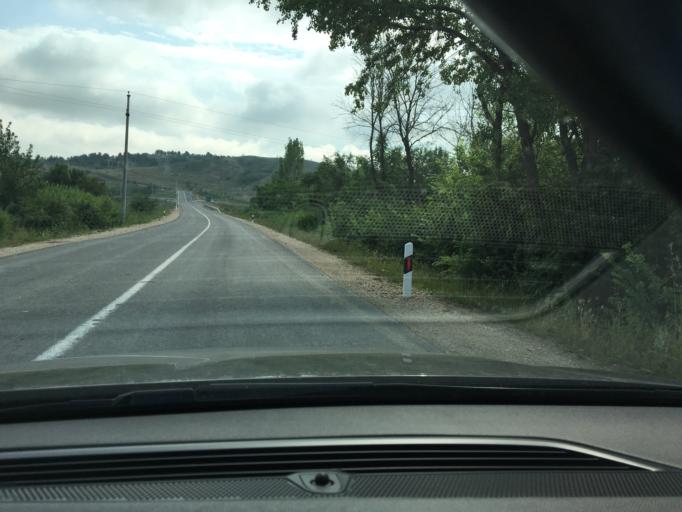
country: MK
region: Sveti Nikole
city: Sveti Nikole
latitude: 41.8543
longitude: 21.9580
